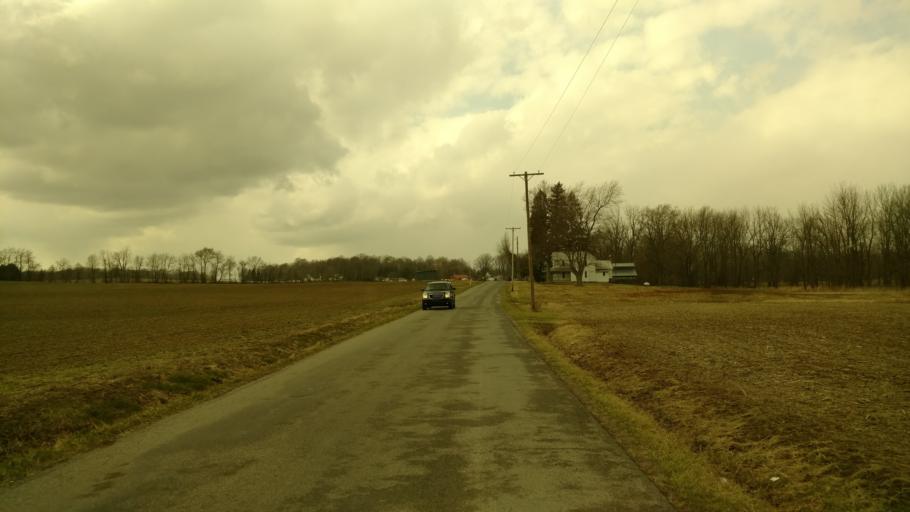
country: US
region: Ohio
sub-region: Richland County
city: Shelby
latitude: 40.8255
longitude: -82.6332
